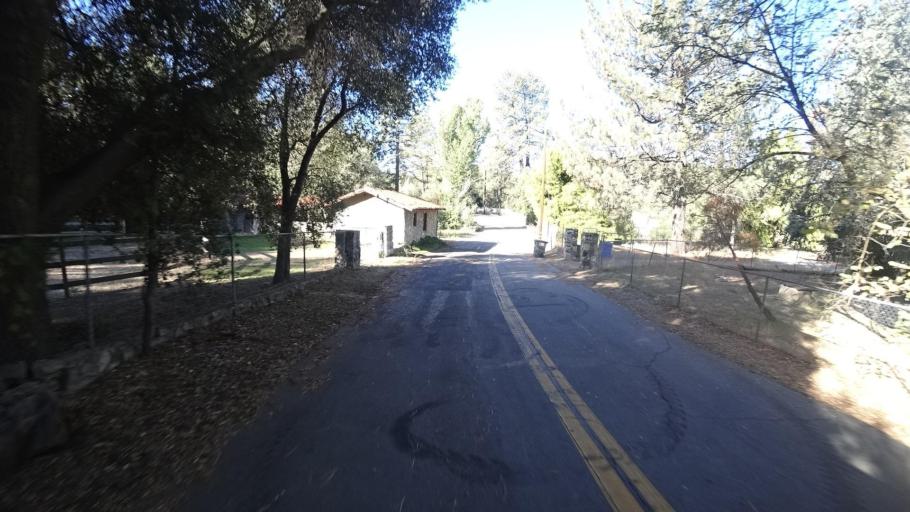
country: US
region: California
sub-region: San Diego County
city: Pine Valley
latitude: 32.8286
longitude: -116.5275
